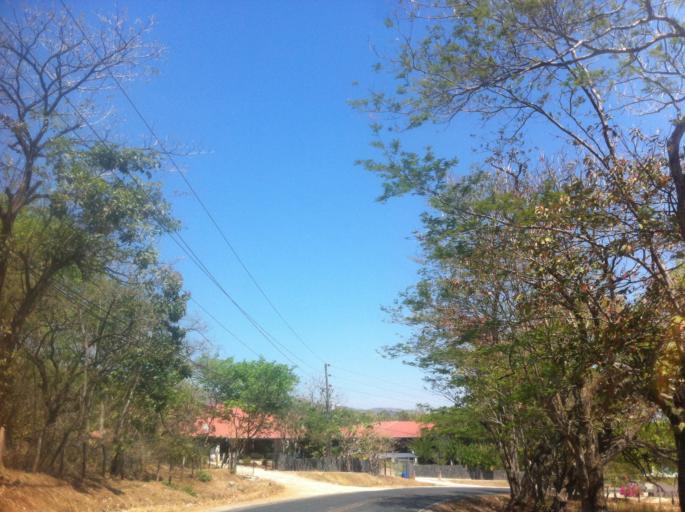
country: CR
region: Guanacaste
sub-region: Canton de Nicoya
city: Nicoya
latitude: 10.1267
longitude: -85.4430
